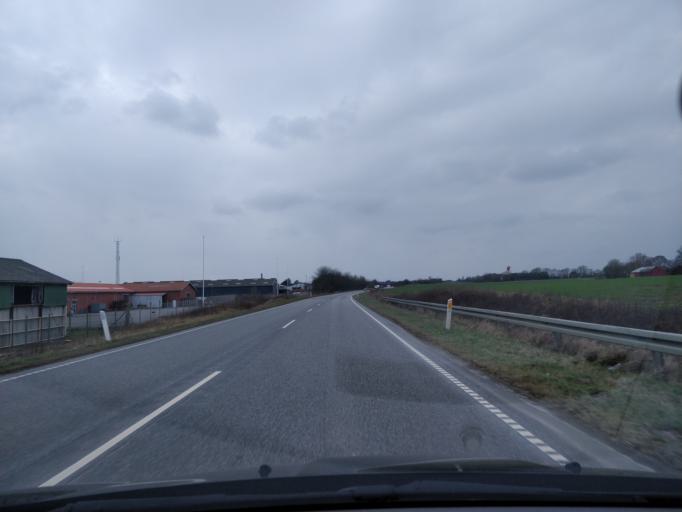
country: DK
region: South Denmark
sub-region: Vejle Kommune
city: Brejning
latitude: 55.6408
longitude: 9.6700
